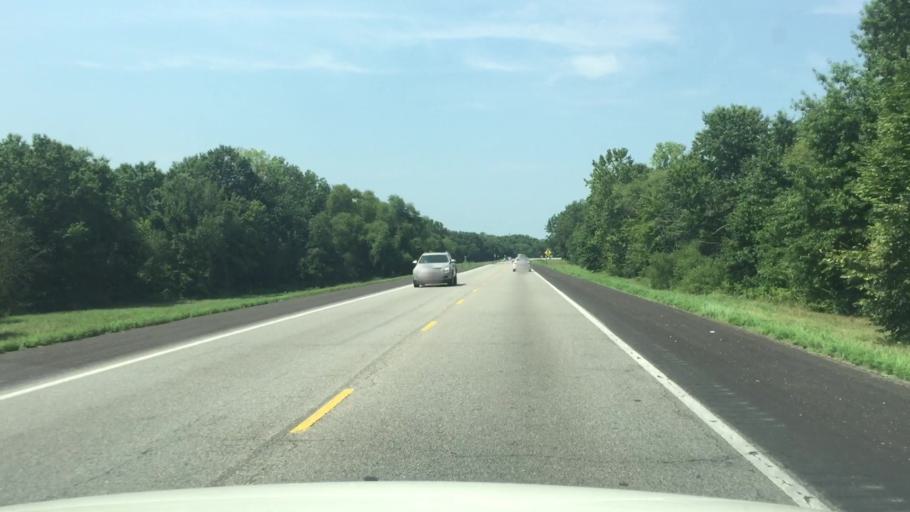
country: US
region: Kansas
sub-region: Crawford County
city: Pittsburg
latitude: 37.4023
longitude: -94.7221
